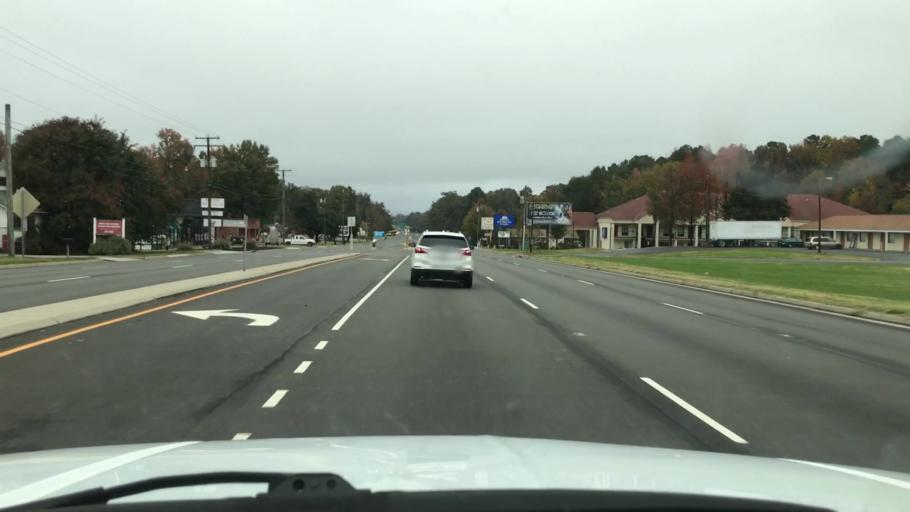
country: US
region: Virginia
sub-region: Henrico County
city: Chamberlayne
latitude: 37.6438
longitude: -77.4601
